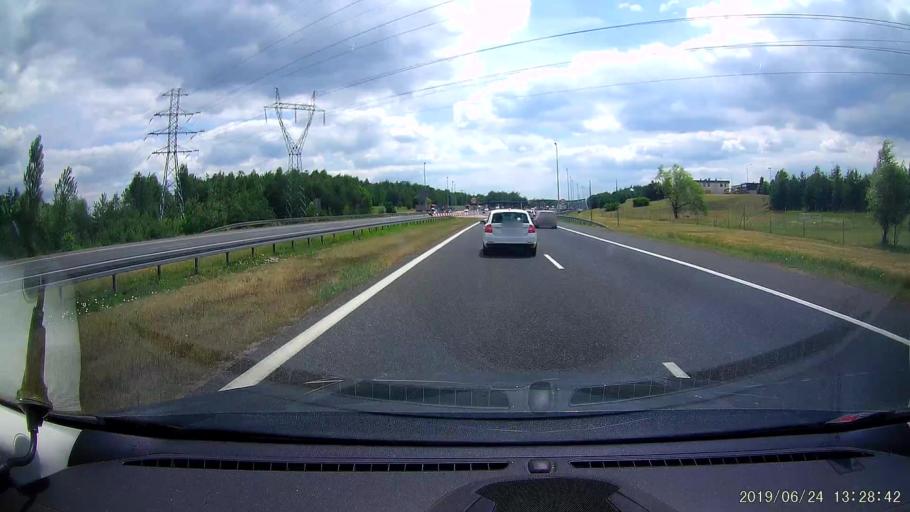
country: PL
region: Silesian Voivodeship
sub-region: Myslowice
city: Myslowice
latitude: 50.2002
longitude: 19.1829
